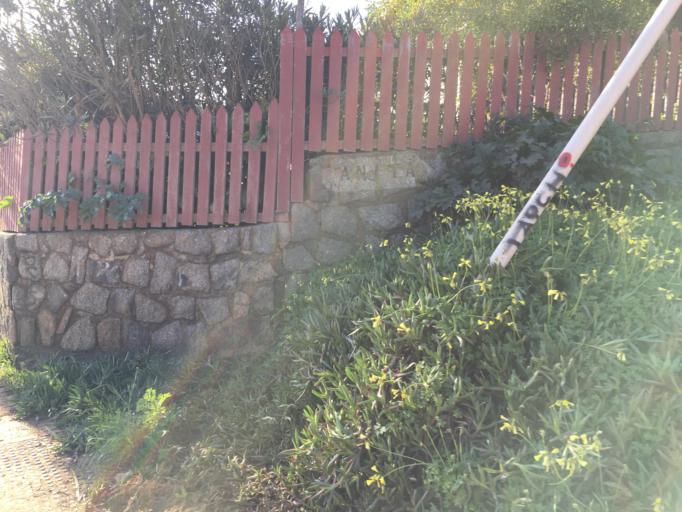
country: CL
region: Valparaiso
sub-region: San Antonio Province
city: El Tabo
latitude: -33.4576
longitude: -71.6598
